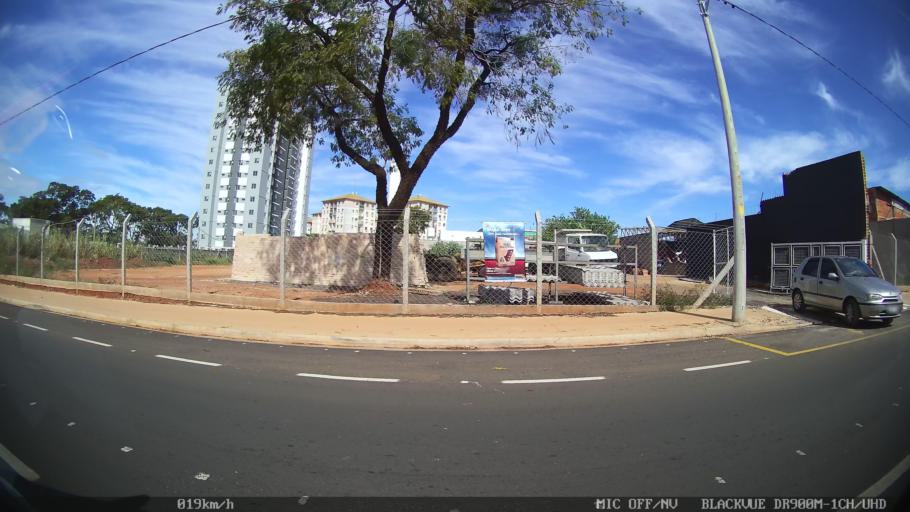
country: BR
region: Sao Paulo
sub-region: Sao Jose Do Rio Preto
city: Sao Jose do Rio Preto
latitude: -20.8251
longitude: -49.3513
